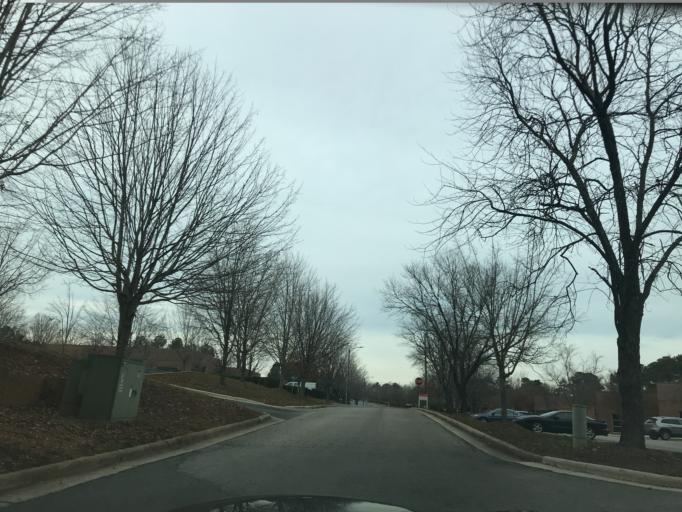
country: US
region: North Carolina
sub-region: Wake County
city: West Raleigh
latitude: 35.7894
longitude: -78.7019
